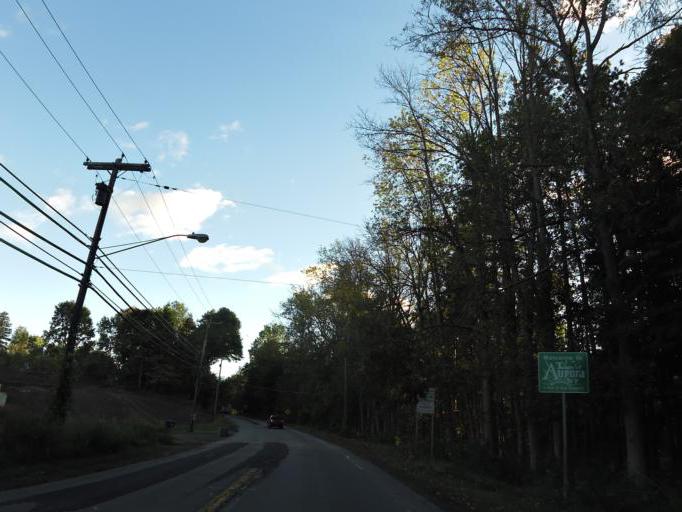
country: US
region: New York
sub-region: Erie County
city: Billington Heights
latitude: 42.7821
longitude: -78.6205
